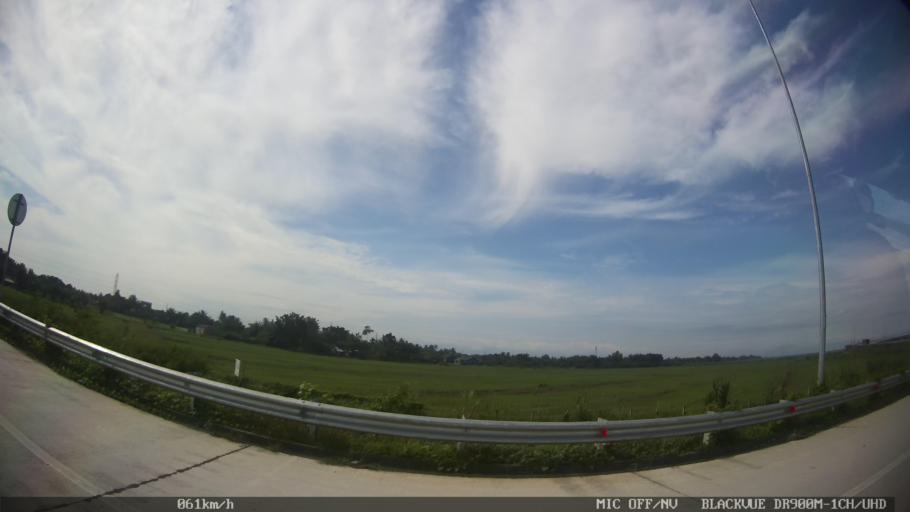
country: ID
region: North Sumatra
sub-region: Kabupaten Langkat
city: Stabat
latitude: 3.7134
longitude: 98.4990
